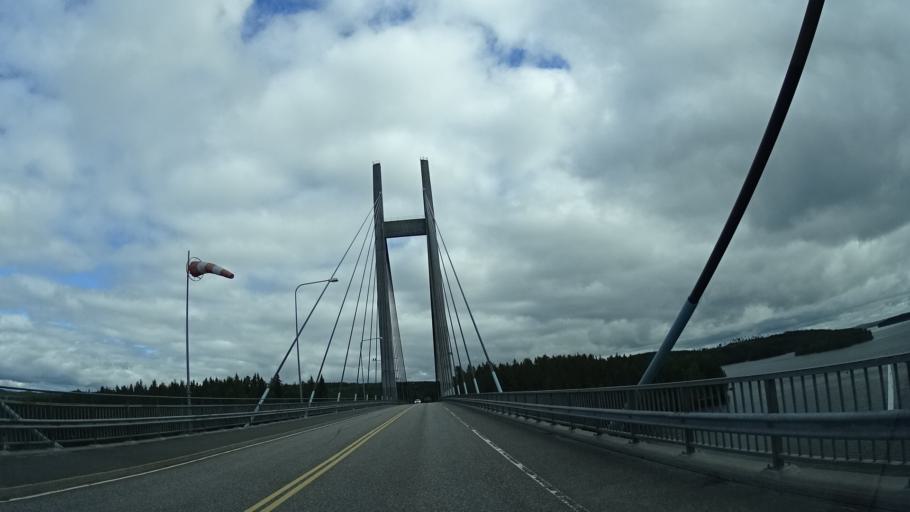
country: FI
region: Central Finland
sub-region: Jyvaeskylae
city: Korpilahti
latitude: 61.9979
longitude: 25.6758
